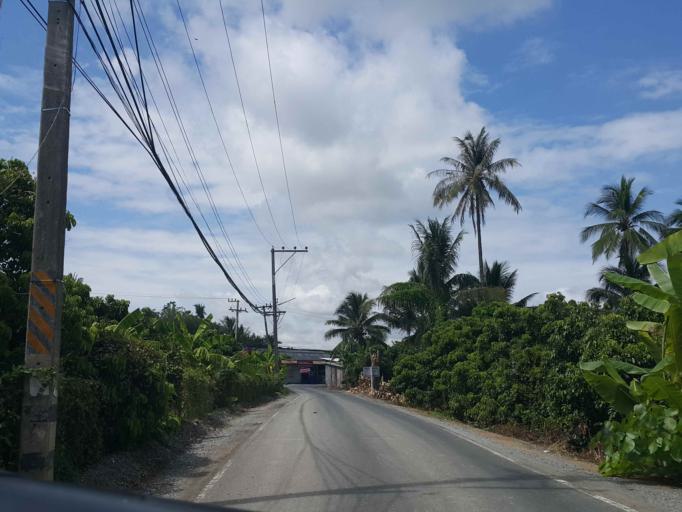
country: TH
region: Chiang Mai
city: Saraphi
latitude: 18.7253
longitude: 99.0498
